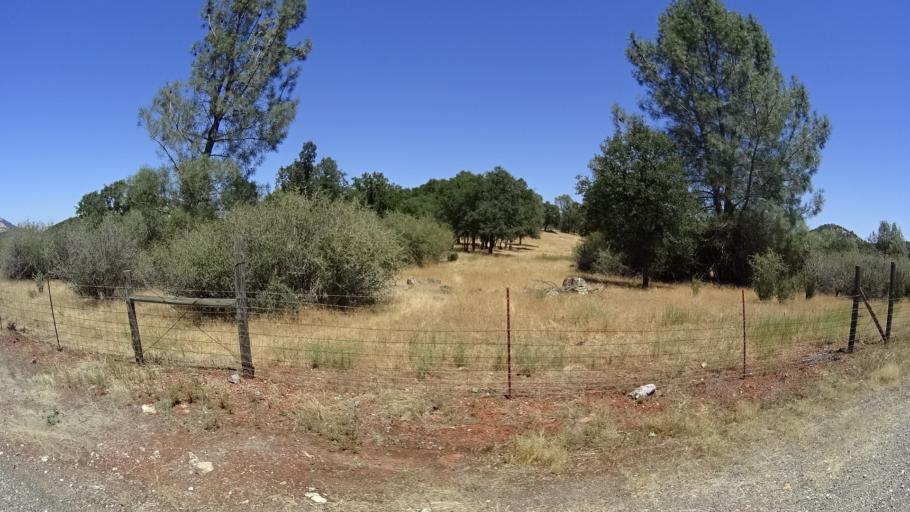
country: US
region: California
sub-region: Calaveras County
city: Copperopolis
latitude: 38.0664
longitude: -120.6574
